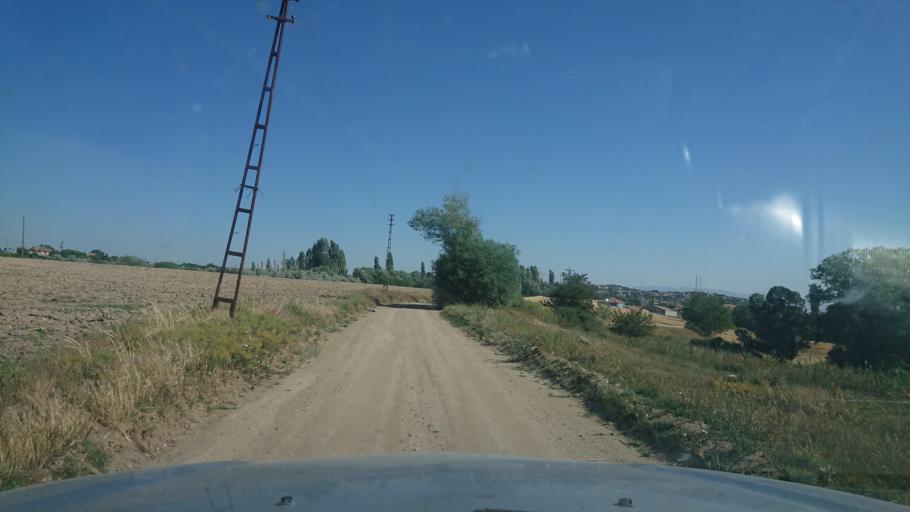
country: TR
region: Aksaray
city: Agacoren
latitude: 38.8588
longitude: 33.9121
